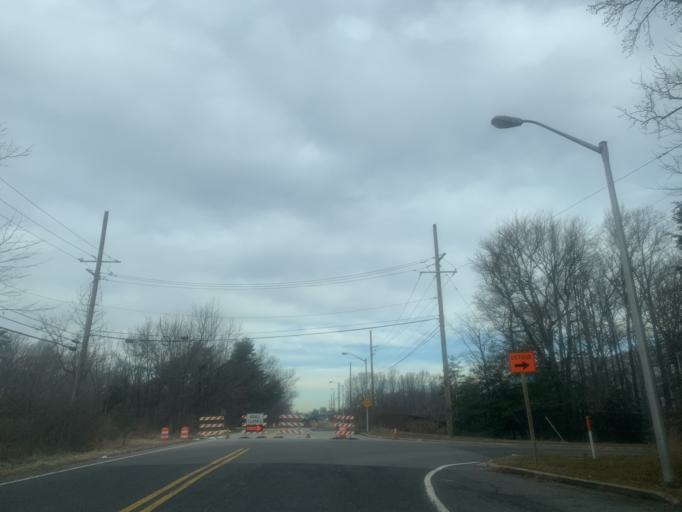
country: US
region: Maryland
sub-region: Prince George's County
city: Andrews AFB
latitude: 38.8241
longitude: -76.8515
